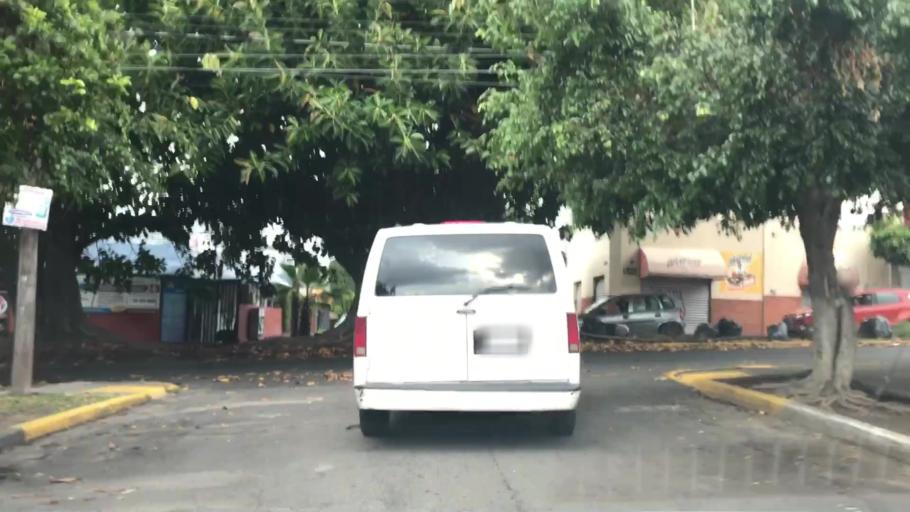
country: MX
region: Jalisco
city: Guadalajara
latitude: 20.6247
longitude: -103.4097
